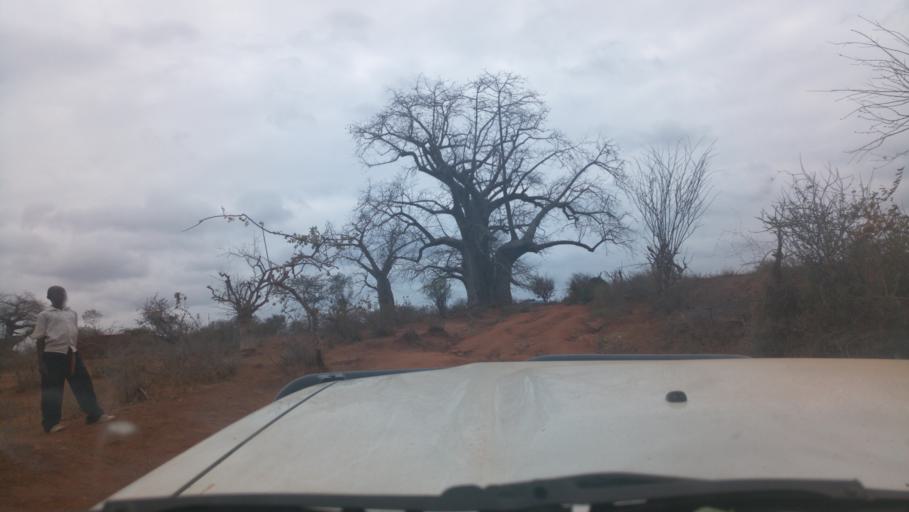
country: KE
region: Makueni
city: Makueni
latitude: -1.9672
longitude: 38.0796
